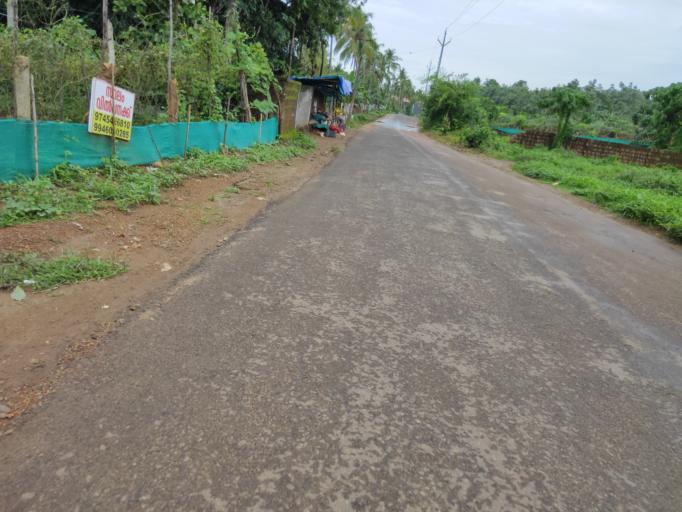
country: IN
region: Kerala
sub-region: Malappuram
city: Manjeri
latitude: 11.2306
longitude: 76.2802
